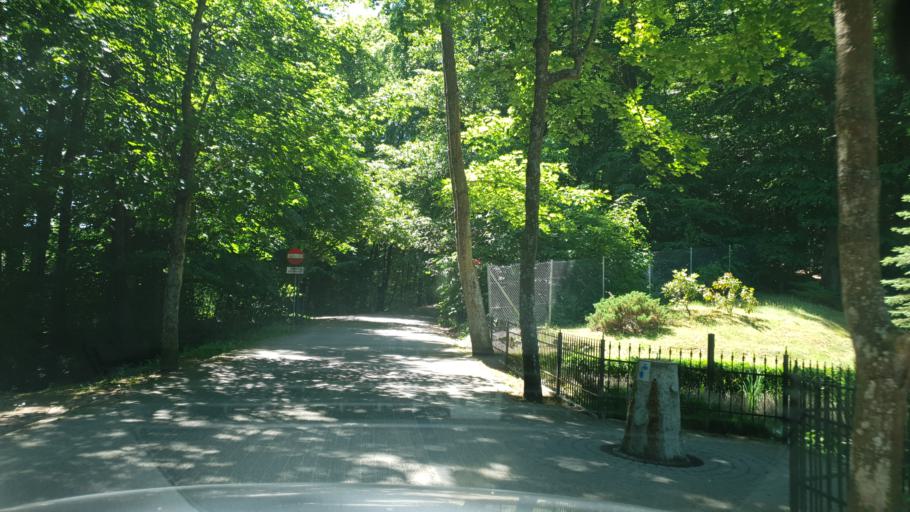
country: PL
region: Pomeranian Voivodeship
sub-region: Gdynia
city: Wielki Kack
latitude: 54.4577
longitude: 18.4847
